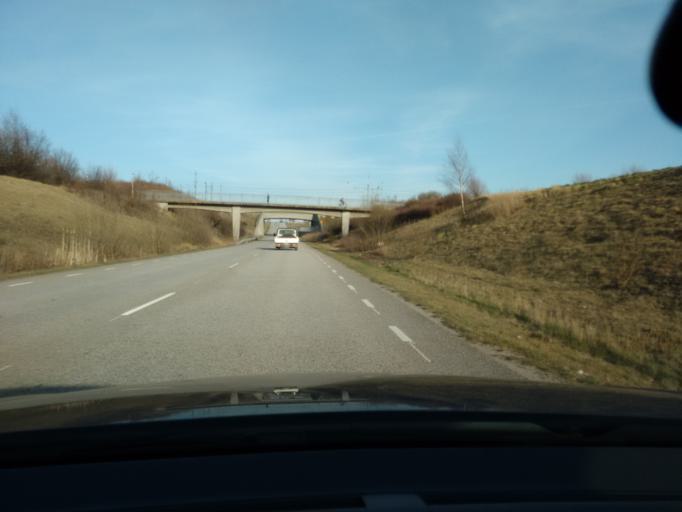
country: SE
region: Skane
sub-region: Lunds Kommun
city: Lund
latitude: 55.7444
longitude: 13.1920
